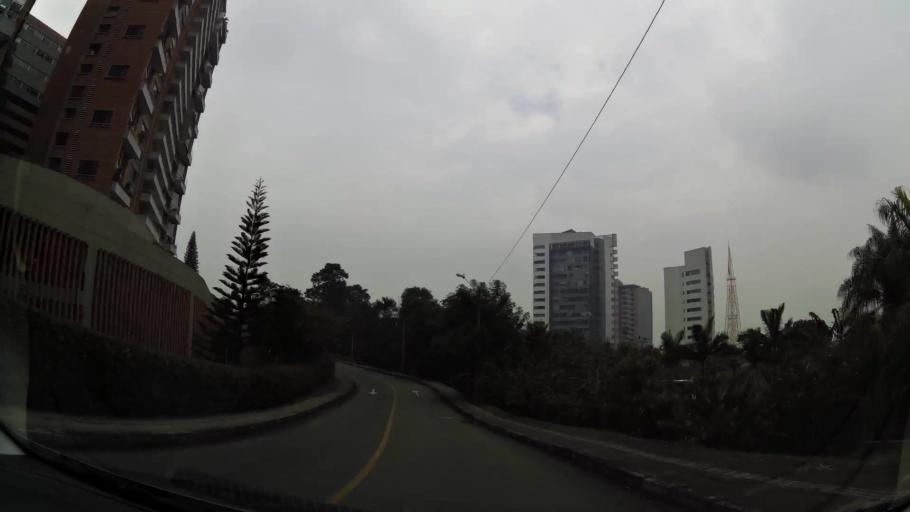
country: CO
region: Antioquia
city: Envigado
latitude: 6.1952
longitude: -75.5570
